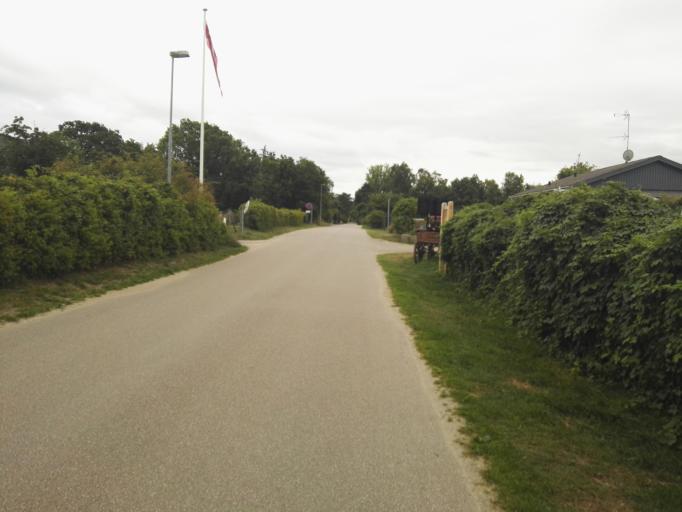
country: DK
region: Zealand
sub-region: Odsherred Kommune
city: Nykobing Sjaelland
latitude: 55.9390
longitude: 11.6633
